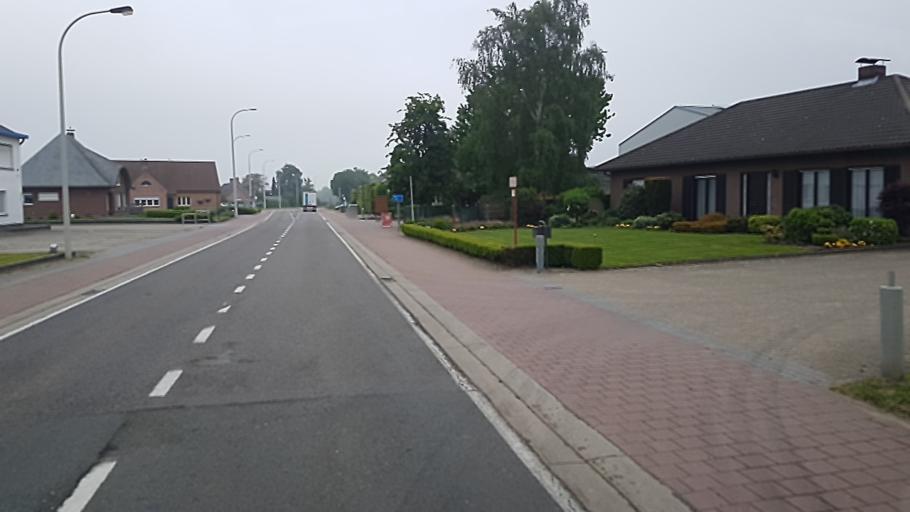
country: BE
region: Flanders
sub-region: Provincie Antwerpen
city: Brecht
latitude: 51.3298
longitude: 4.6754
